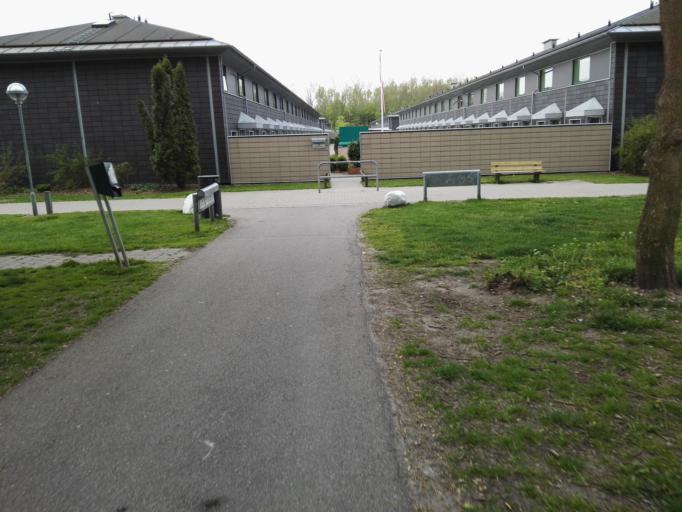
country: DK
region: Capital Region
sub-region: Ballerup Kommune
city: Ballerup
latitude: 55.7259
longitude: 12.3394
